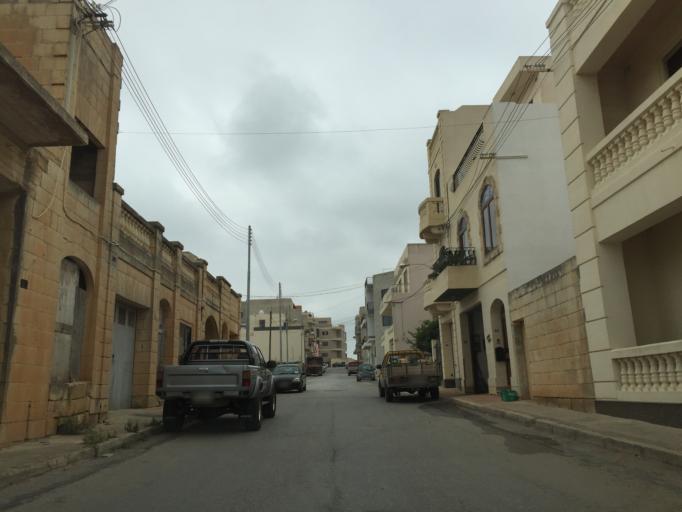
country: MT
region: L-Imgarr
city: Imgarr
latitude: 35.9210
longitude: 14.3684
